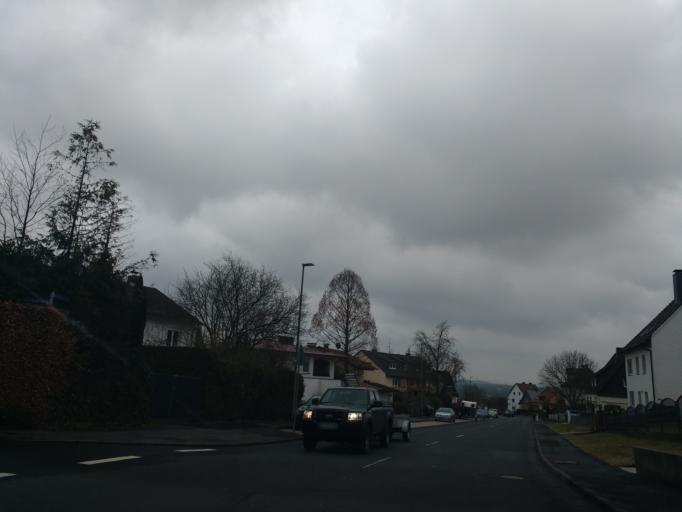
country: DE
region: Hesse
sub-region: Regierungsbezirk Kassel
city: Baunatal
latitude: 51.2851
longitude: 9.4191
